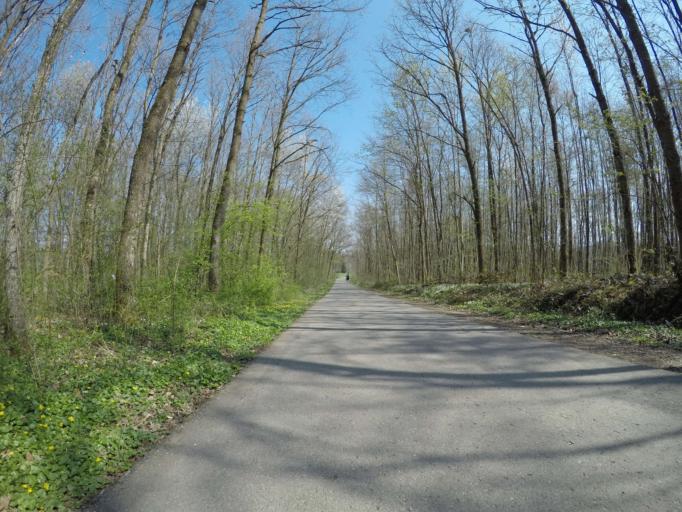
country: DE
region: Baden-Wuerttemberg
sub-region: Tuebingen Region
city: Wannweil
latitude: 48.4852
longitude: 9.1655
